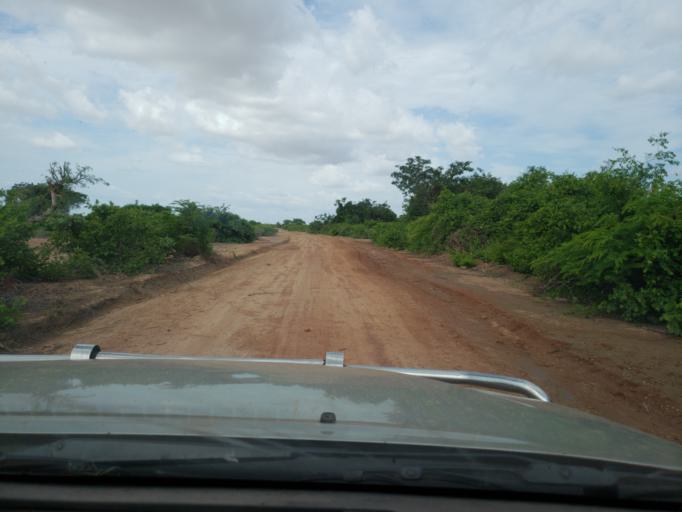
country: ML
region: Segou
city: Bla
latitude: 12.7078
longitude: -5.7051
